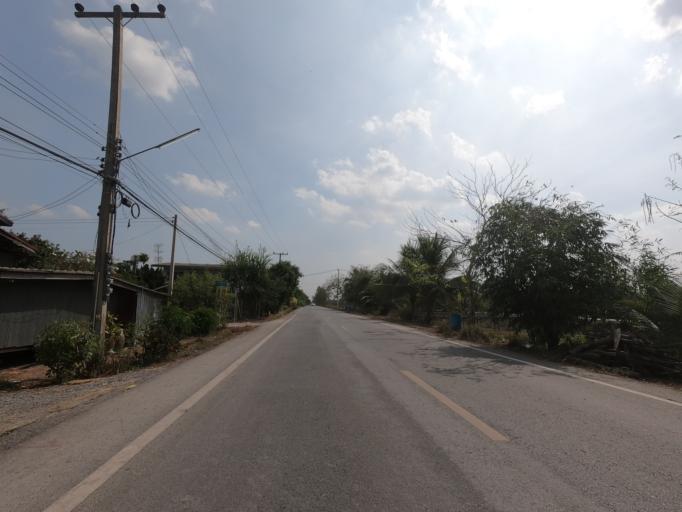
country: TH
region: Pathum Thani
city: Nong Suea
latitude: 14.1481
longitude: 100.8464
